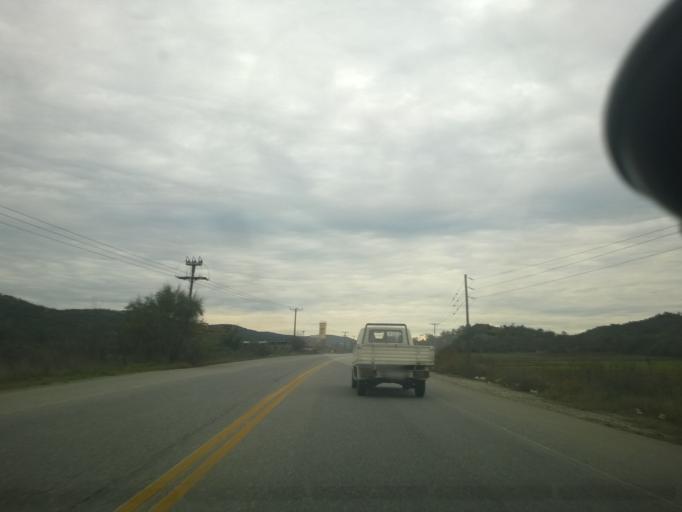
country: GR
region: Central Macedonia
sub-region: Nomos Pellis
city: Apsalos
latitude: 40.8833
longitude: 22.0800
